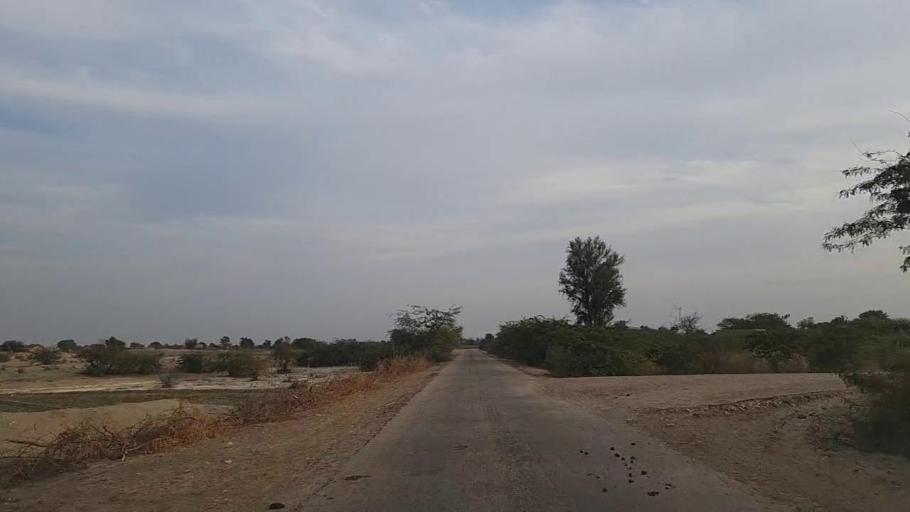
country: PK
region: Sindh
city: Jam Sahib
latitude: 26.4797
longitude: 68.5630
